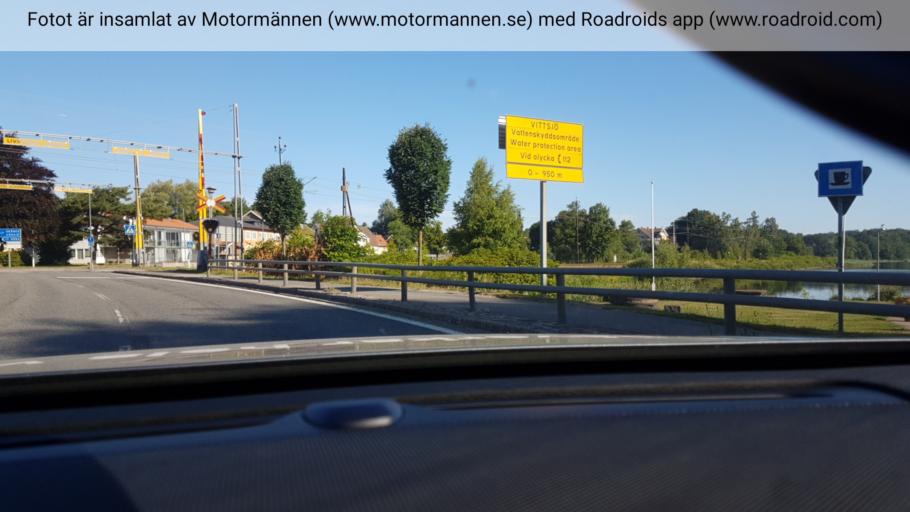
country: SE
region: Skane
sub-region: Hassleholms Kommun
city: Bjarnum
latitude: 56.3430
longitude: 13.6639
